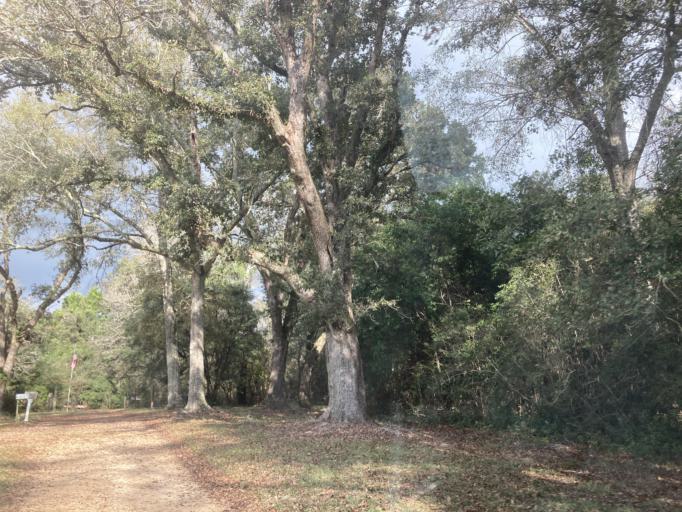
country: US
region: Mississippi
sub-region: Stone County
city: Wiggins
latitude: 30.8574
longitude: -89.3241
